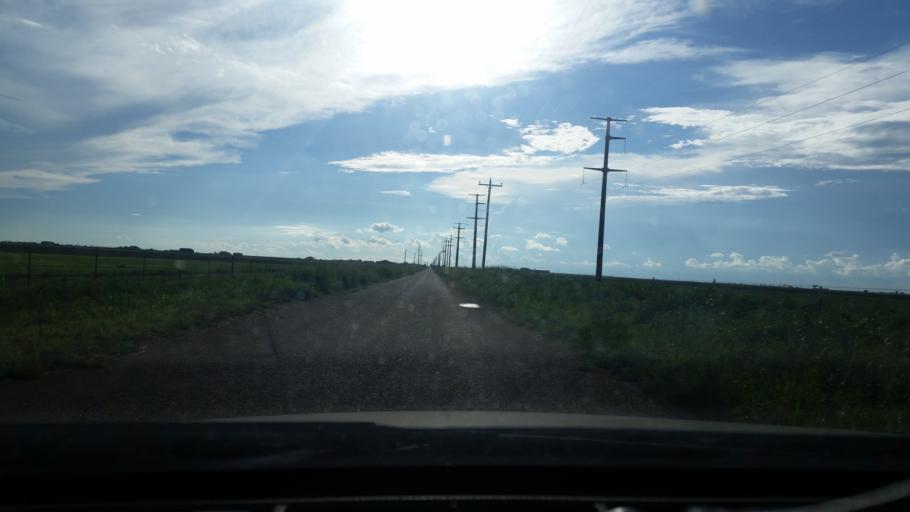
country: US
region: New Mexico
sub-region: Curry County
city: Clovis
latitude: 34.5065
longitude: -103.1794
